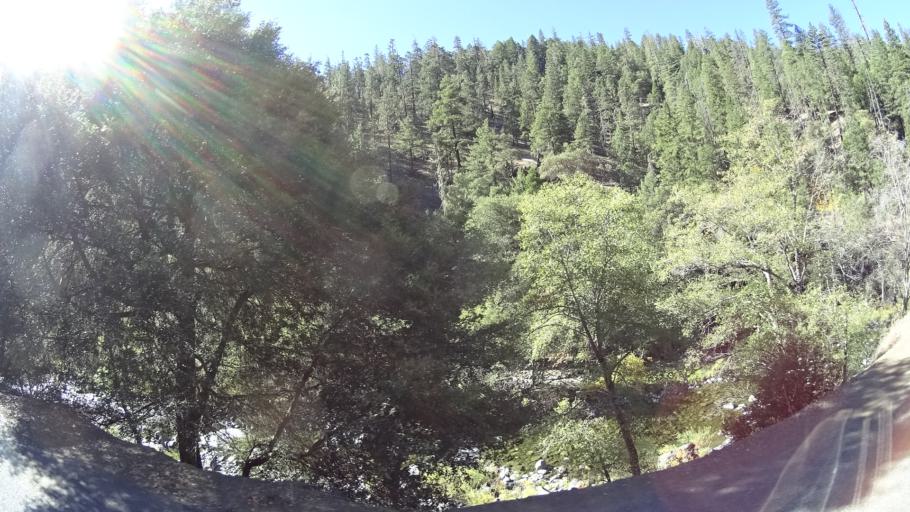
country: US
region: California
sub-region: Humboldt County
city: Willow Creek
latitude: 41.2012
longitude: -123.2226
